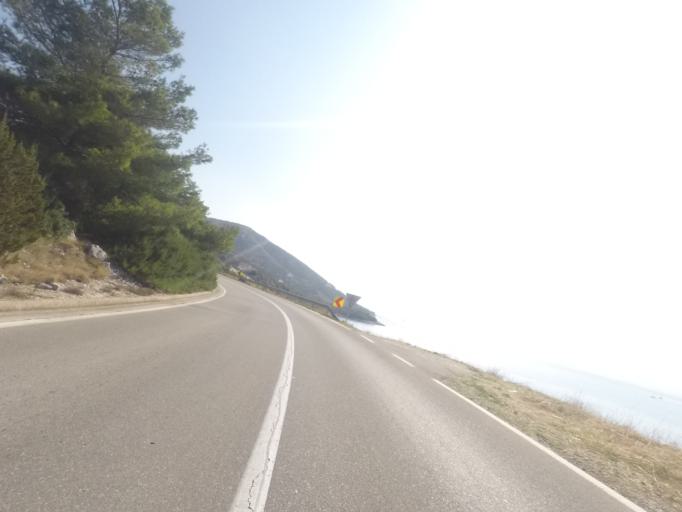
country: HR
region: Splitsko-Dalmatinska
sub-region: Grad Hvar
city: Hvar
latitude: 43.1609
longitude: 16.4901
